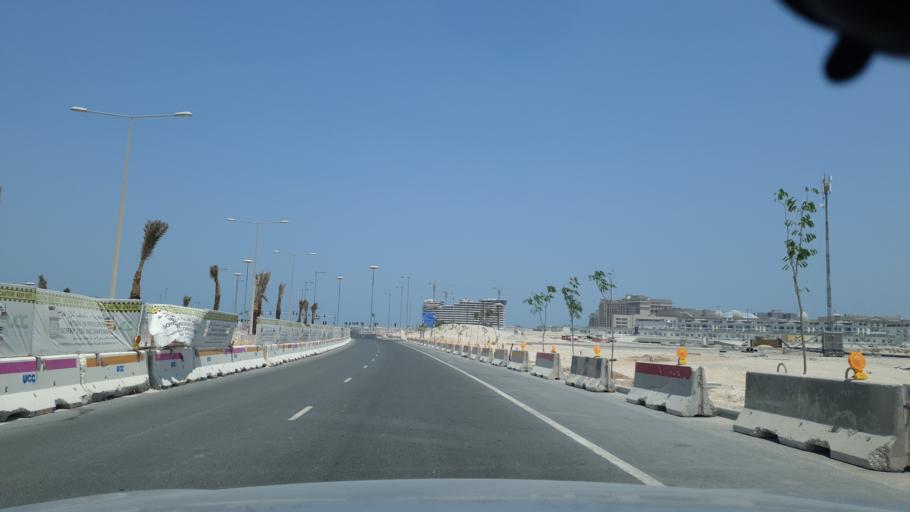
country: QA
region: Baladiyat Umm Salal
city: Umm Salal Muhammad
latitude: 25.4069
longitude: 51.5090
